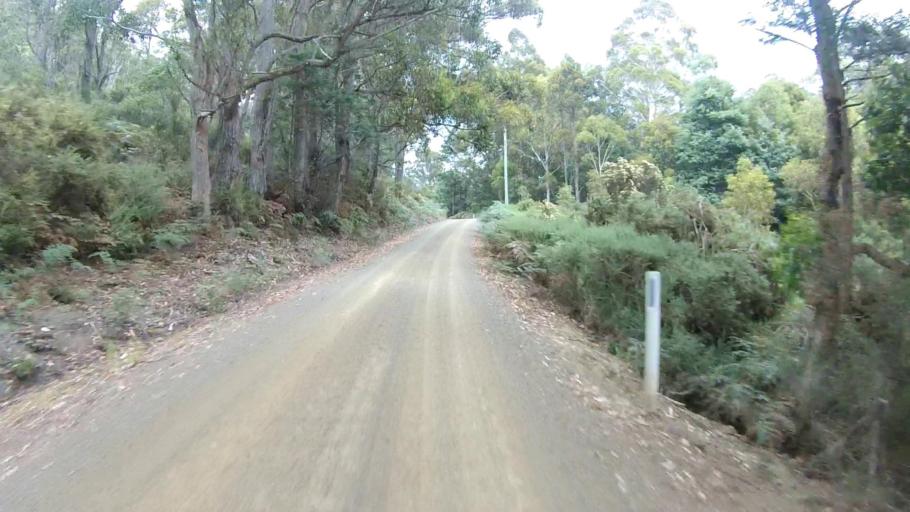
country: AU
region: Tasmania
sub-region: Huon Valley
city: Cygnet
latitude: -43.2236
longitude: 147.1725
